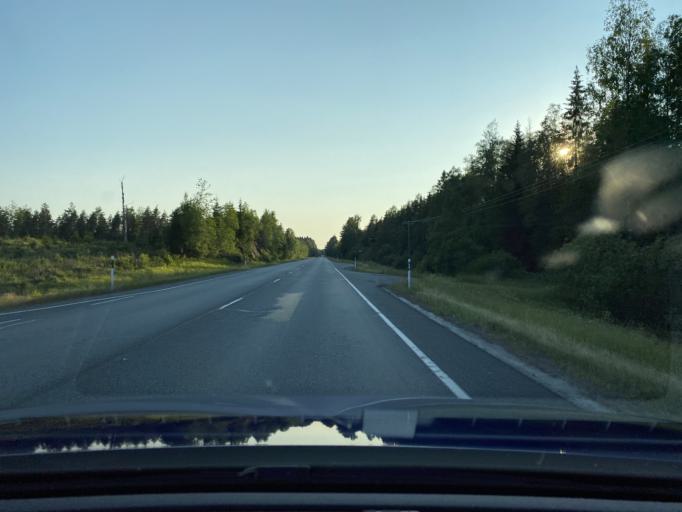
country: FI
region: Haeme
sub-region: Forssa
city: Tammela
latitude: 60.8260
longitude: 23.9523
